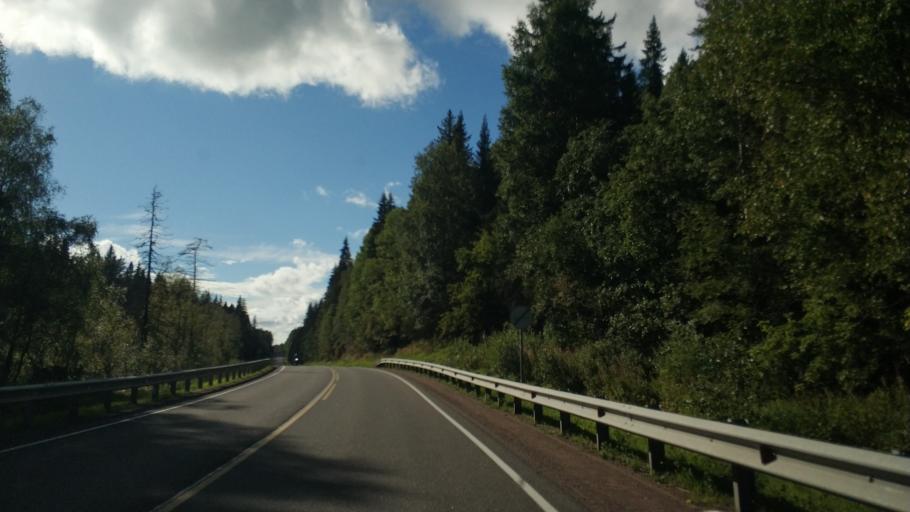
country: RU
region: Republic of Karelia
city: Sortavala
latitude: 61.6565
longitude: 30.6393
